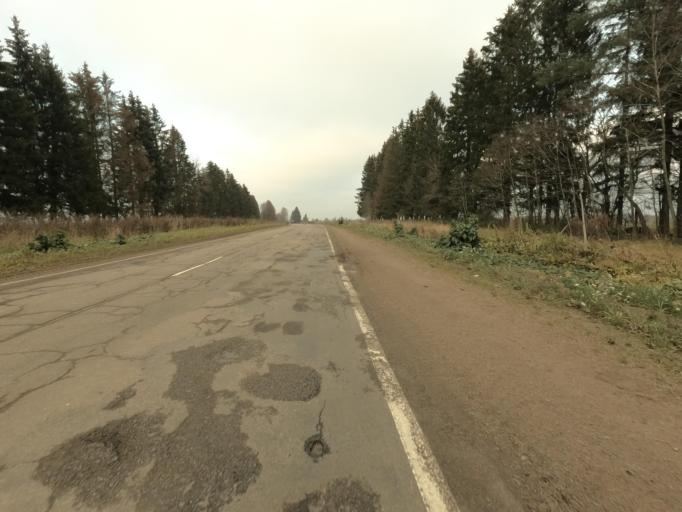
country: RU
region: Leningrad
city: Mga
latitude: 59.7799
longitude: 31.0248
